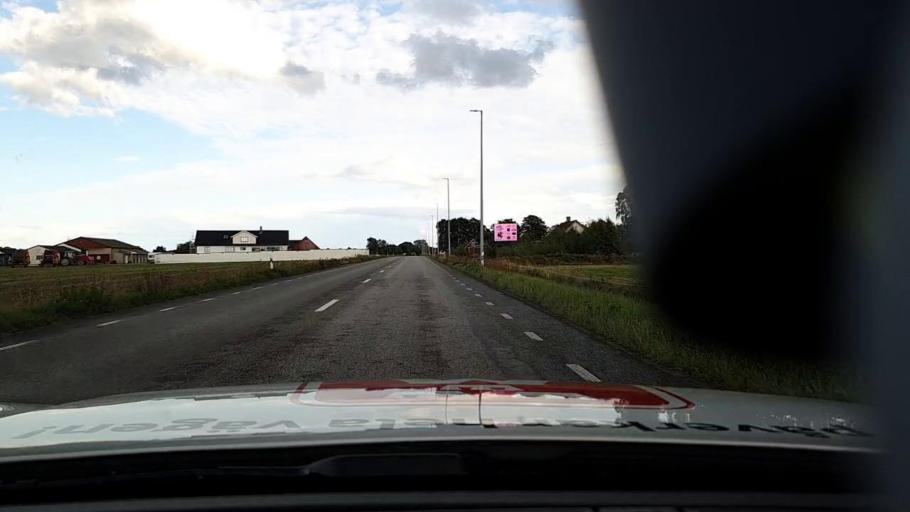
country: SE
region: Blekinge
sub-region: Solvesborgs Kommun
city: Soelvesborg
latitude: 56.0537
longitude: 14.6419
